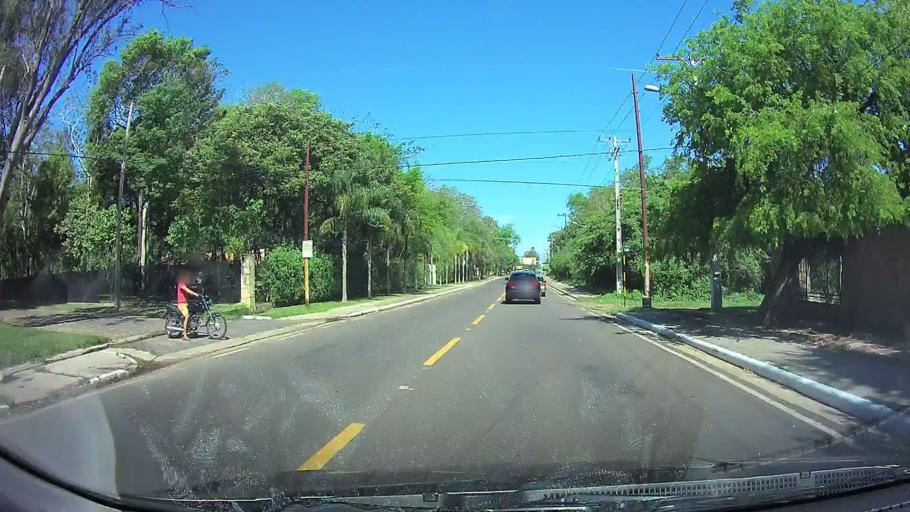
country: PY
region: Cordillera
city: San Bernardino
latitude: -25.2887
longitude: -57.3124
